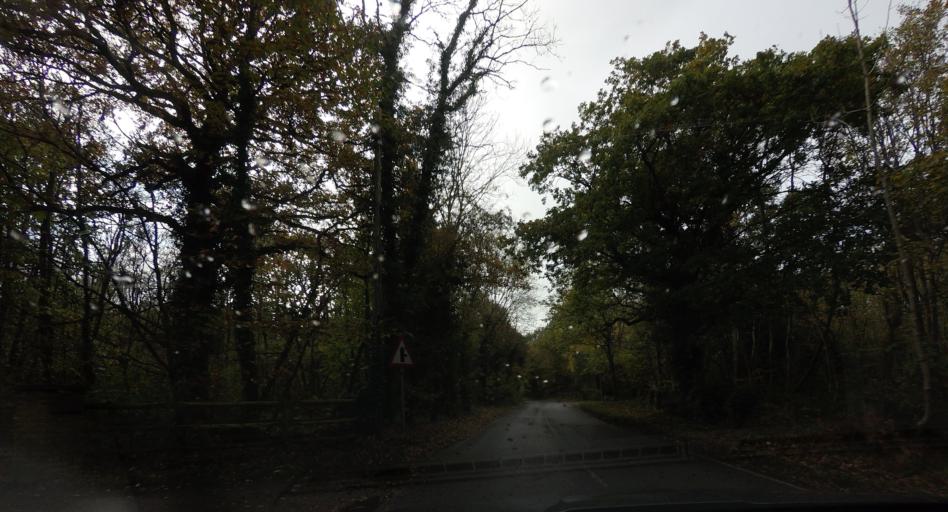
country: GB
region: England
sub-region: Medway
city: Cuxton
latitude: 51.4050
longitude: 0.4279
